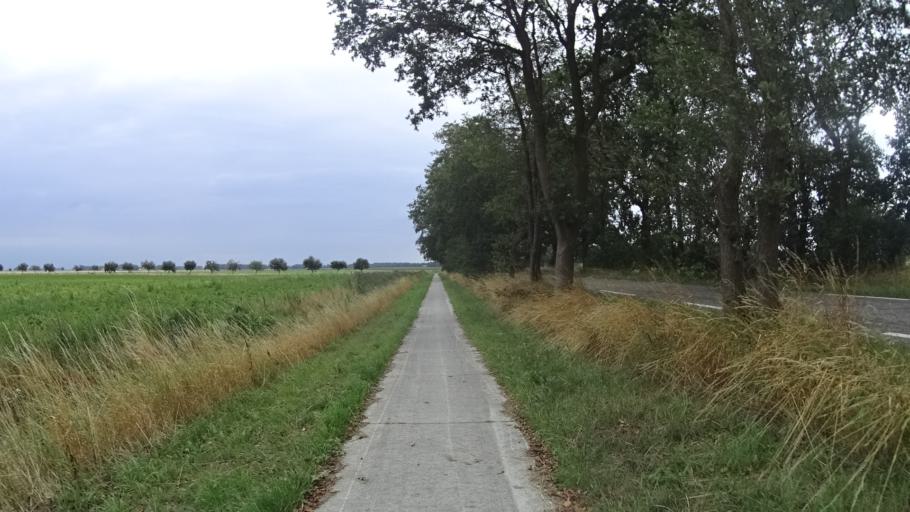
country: NL
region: Groningen
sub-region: Gemeente Slochteren
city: Slochteren
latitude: 53.2072
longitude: 6.8339
